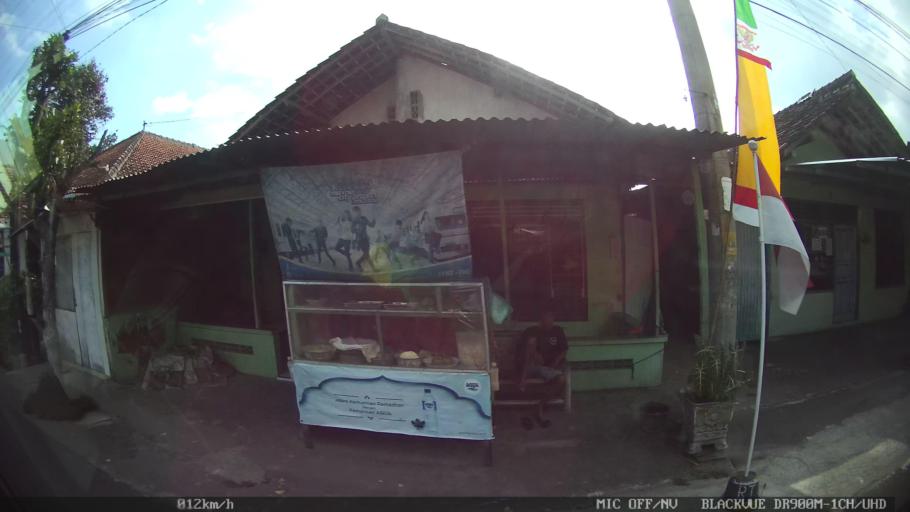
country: ID
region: Daerah Istimewa Yogyakarta
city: Gamping Lor
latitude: -7.7994
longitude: 110.3357
